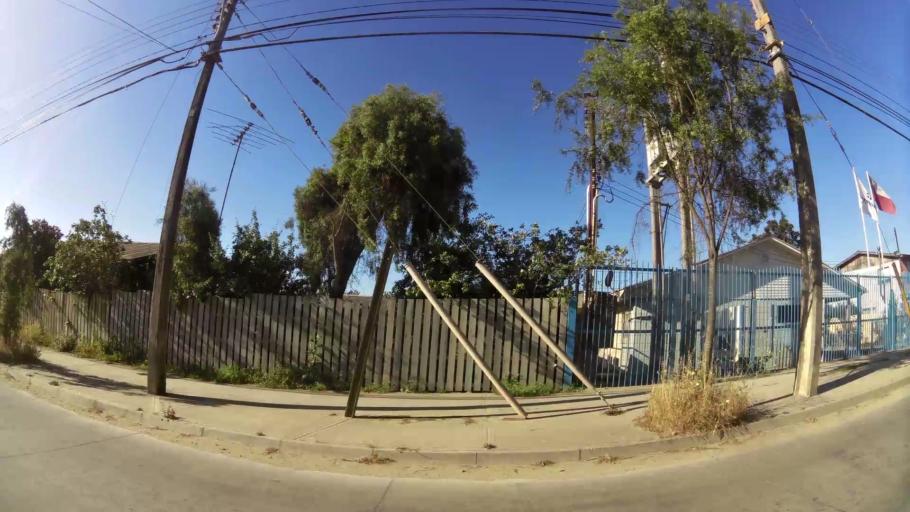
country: CL
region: Valparaiso
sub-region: Provincia de Valparaiso
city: Vina del Mar
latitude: -33.1158
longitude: -71.5638
